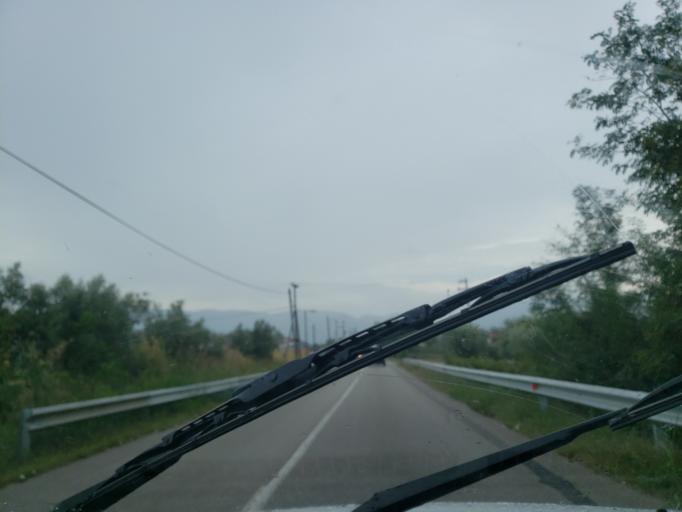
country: GR
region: Central Greece
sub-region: Nomos Fthiotidos
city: Anthili
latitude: 38.8548
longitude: 22.4403
